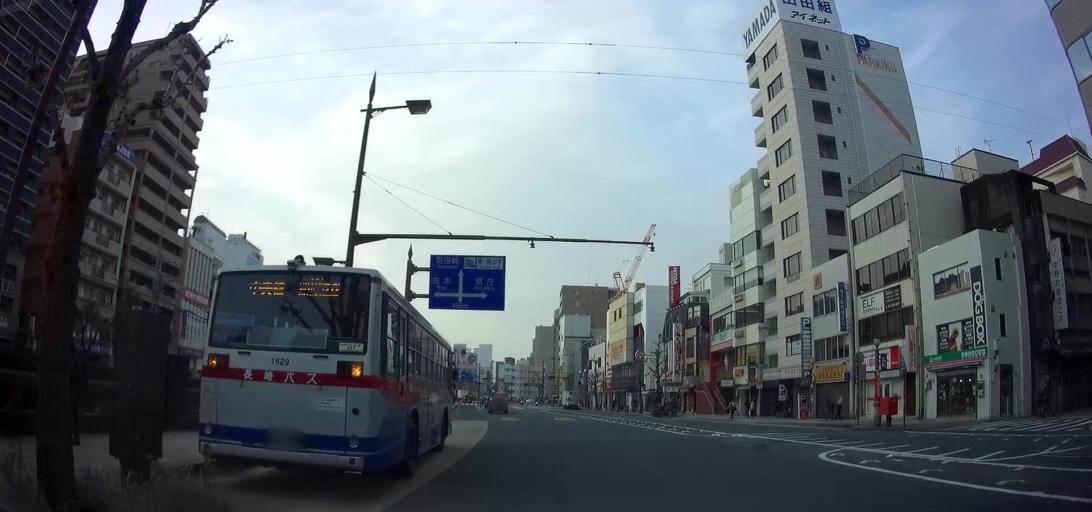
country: JP
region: Nagasaki
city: Nagasaki-shi
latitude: 32.7459
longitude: 129.8769
